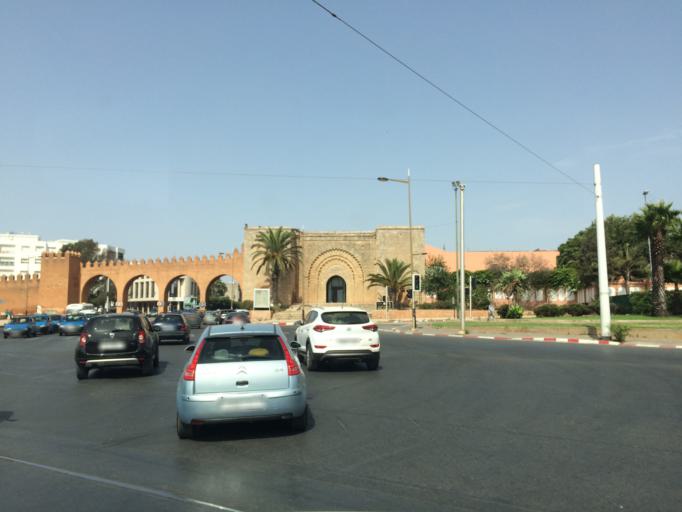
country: MA
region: Rabat-Sale-Zemmour-Zaer
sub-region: Rabat
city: Rabat
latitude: 34.0125
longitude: -6.8387
